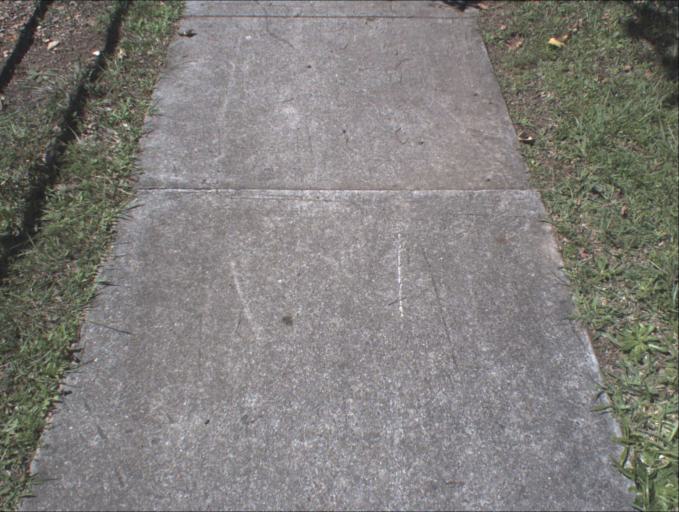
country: AU
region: Queensland
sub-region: Logan
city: Beenleigh
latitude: -27.7006
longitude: 153.1740
